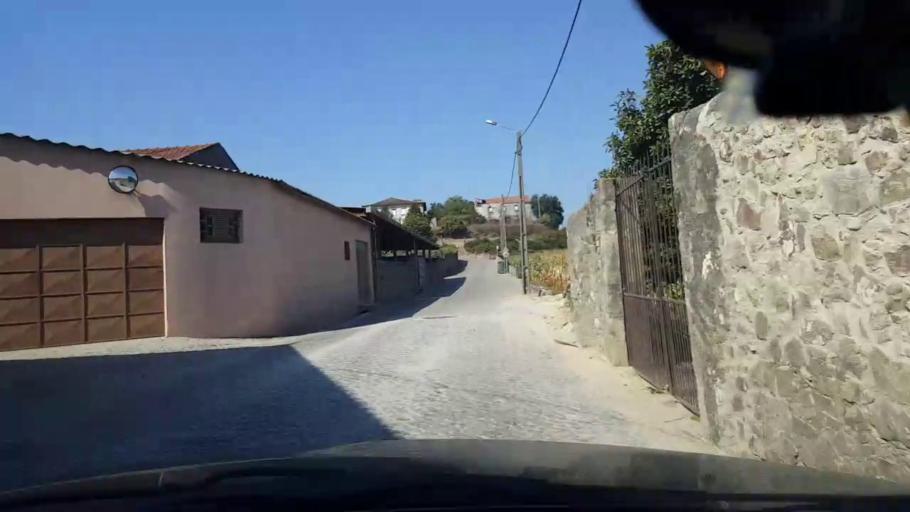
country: PT
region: Porto
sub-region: Povoa de Varzim
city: Pedroso
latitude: 41.3990
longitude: -8.6886
